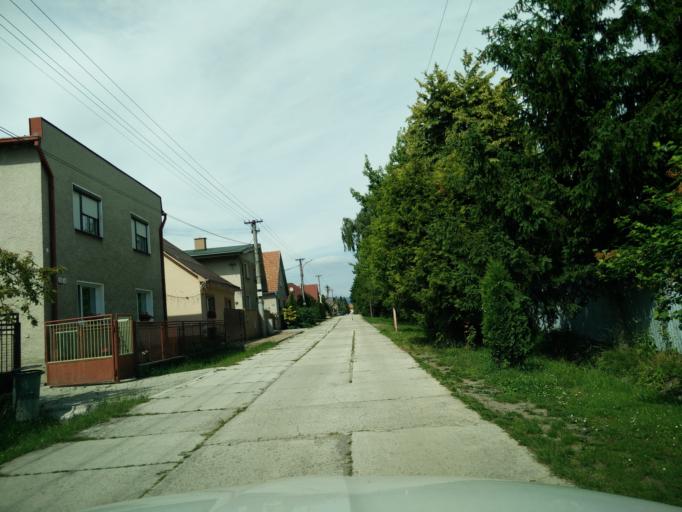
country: SK
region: Nitriansky
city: Prievidza
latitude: 48.8147
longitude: 18.6181
